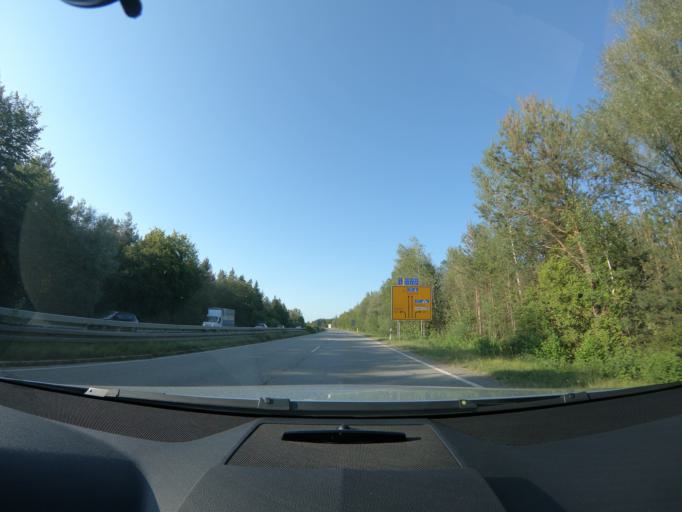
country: DE
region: Bavaria
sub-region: Upper Bavaria
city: Oberschleissheim
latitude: 48.2452
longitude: 11.6021
